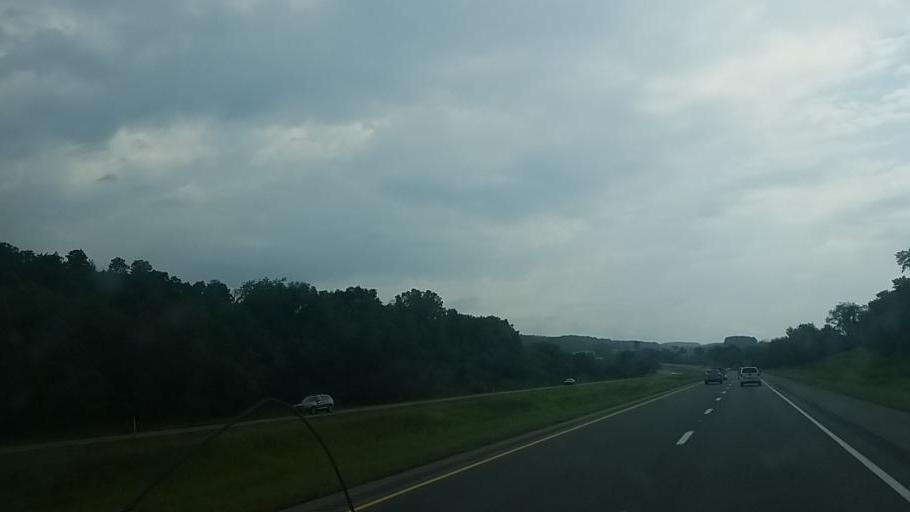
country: US
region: Pennsylvania
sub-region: Juniata County
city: Mifflintown
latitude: 40.5441
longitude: -77.3228
